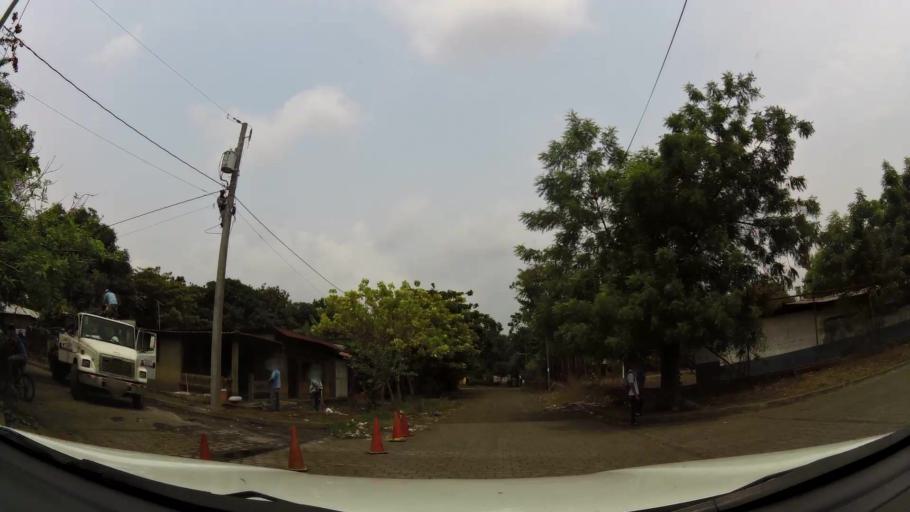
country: NI
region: Chinandega
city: Chinandega
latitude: 12.6505
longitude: -87.1229
